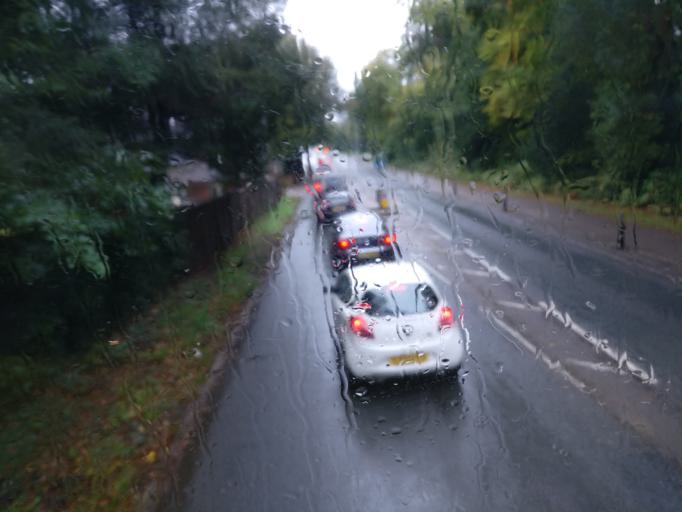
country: GB
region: England
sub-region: Hampshire
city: Farnborough
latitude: 51.2993
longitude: -0.7534
